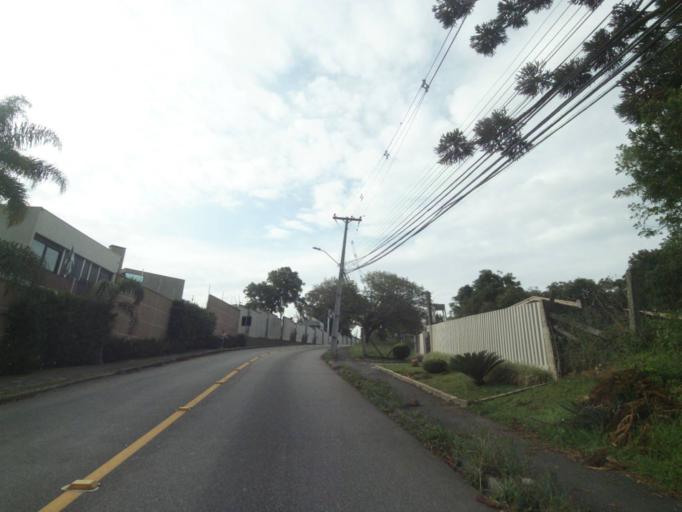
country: BR
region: Parana
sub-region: Curitiba
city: Curitiba
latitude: -25.4124
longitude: -49.3117
